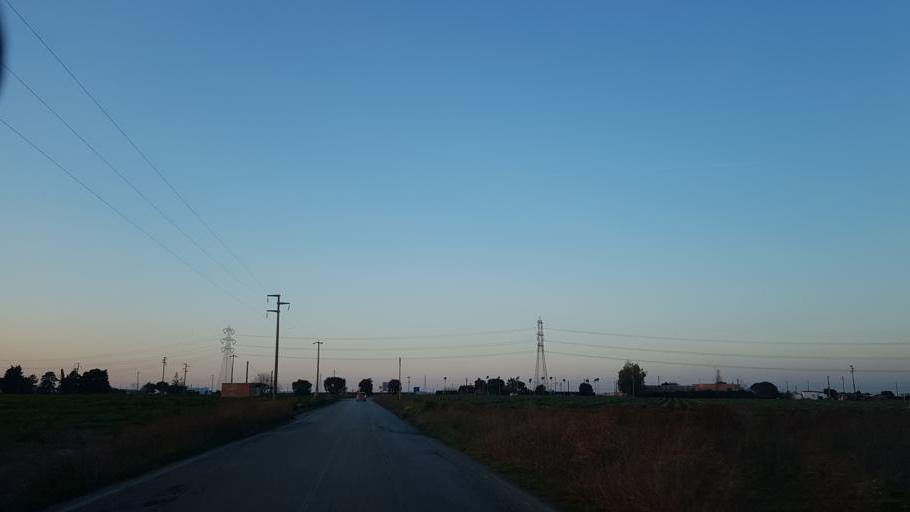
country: IT
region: Apulia
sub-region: Provincia di Brindisi
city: La Rosa
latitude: 40.5881
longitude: 17.9448
